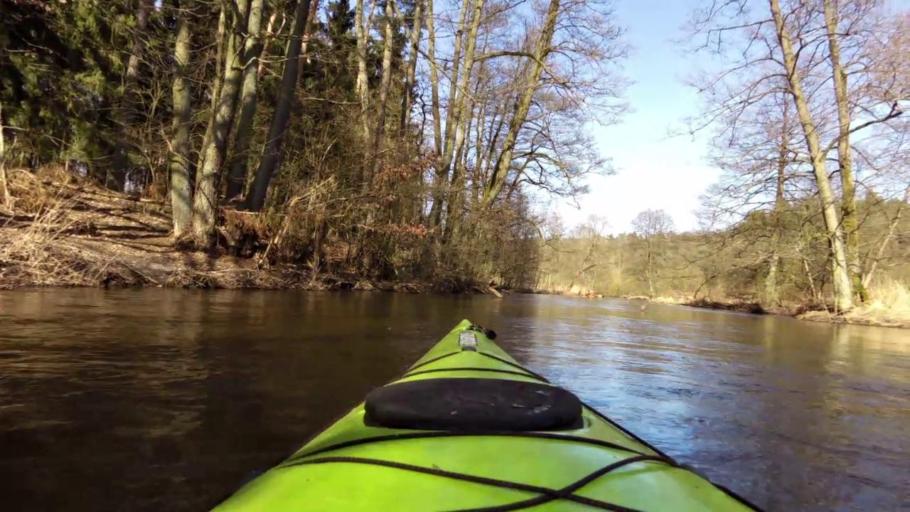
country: PL
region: West Pomeranian Voivodeship
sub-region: Powiat lobeski
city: Lobez
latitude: 53.6840
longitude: 15.5605
